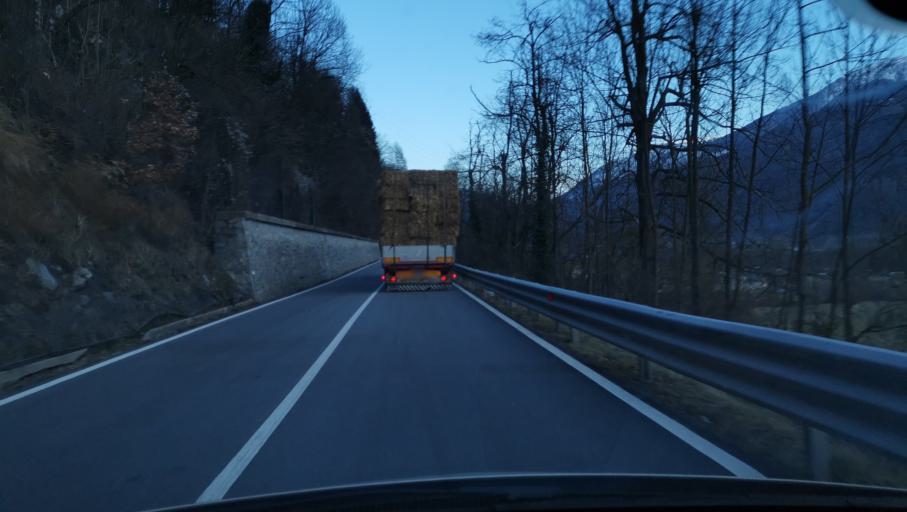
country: IT
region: Piedmont
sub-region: Provincia di Cuneo
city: Demonte
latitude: 44.3157
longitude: 7.2690
